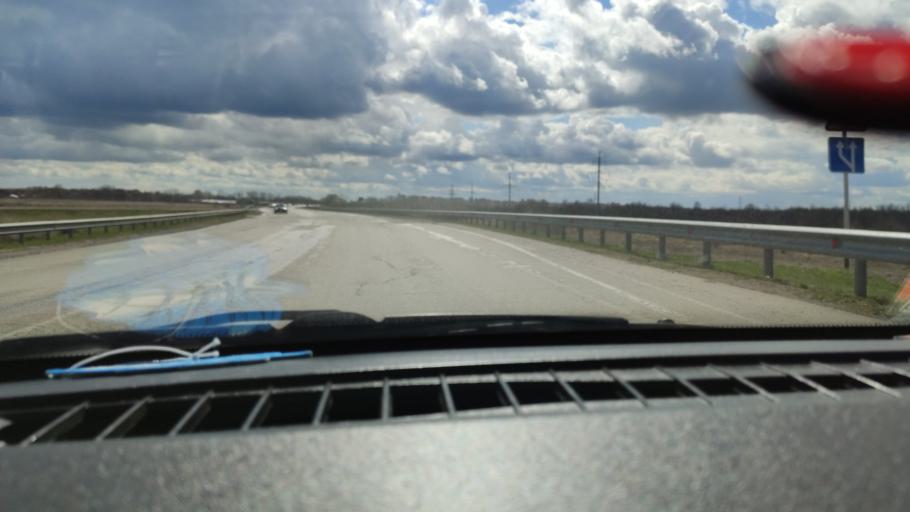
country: RU
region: Samara
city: Tol'yatti
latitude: 53.6660
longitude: 49.4195
